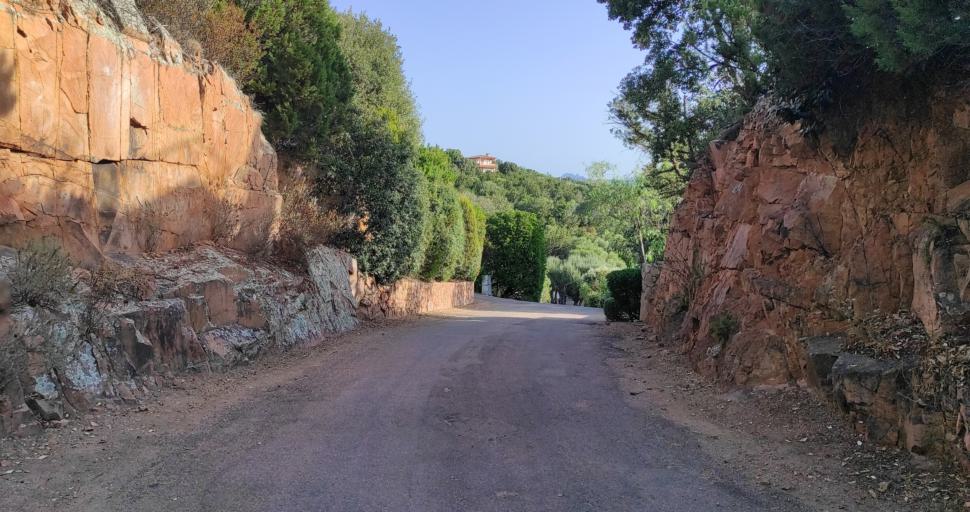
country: FR
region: Corsica
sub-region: Departement de la Corse-du-Sud
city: Porto-Vecchio
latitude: 41.6213
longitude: 9.3509
